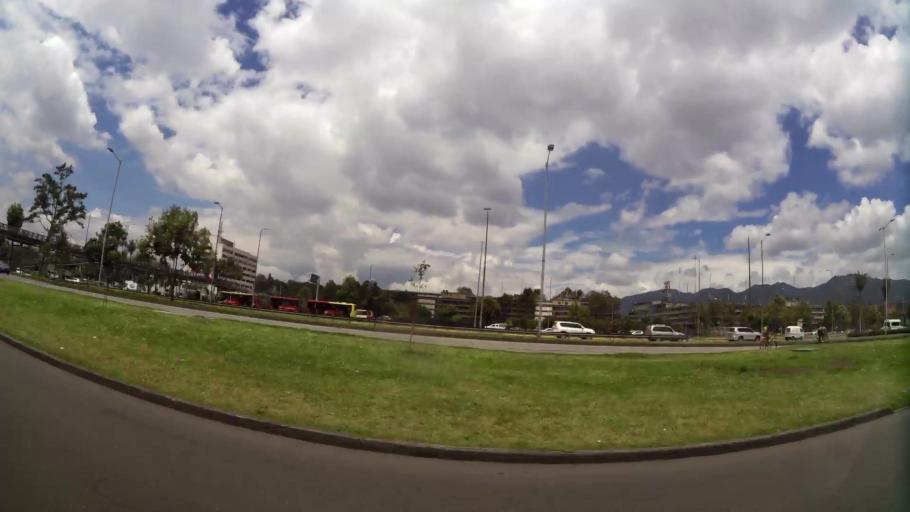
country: CO
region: Bogota D.C.
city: Bogota
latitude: 4.6449
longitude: -74.0985
